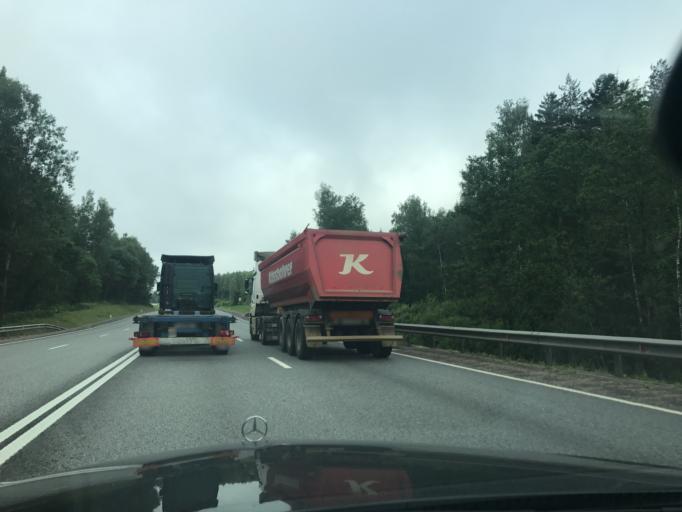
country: RU
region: Smolensk
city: Vyaz'ma
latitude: 55.3174
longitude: 34.5381
